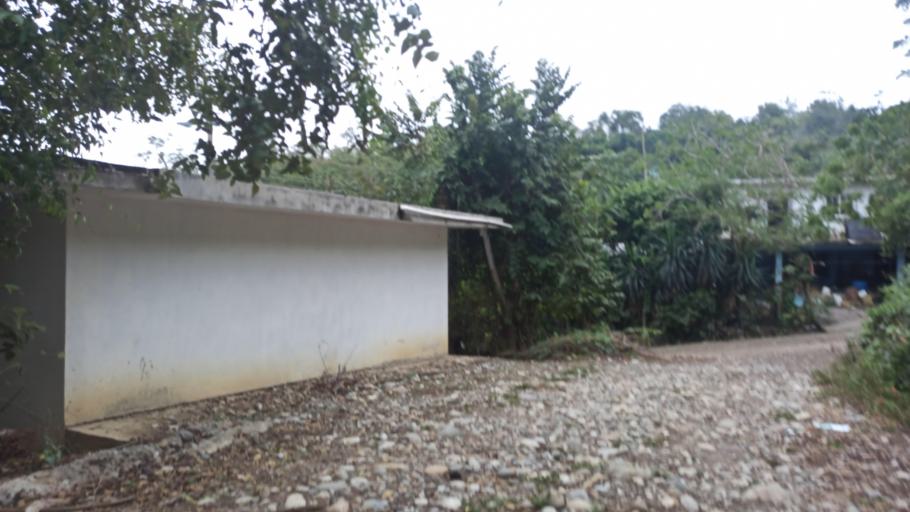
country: MX
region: Veracruz
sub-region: Papantla
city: El Chote
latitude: 20.3836
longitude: -97.3550
